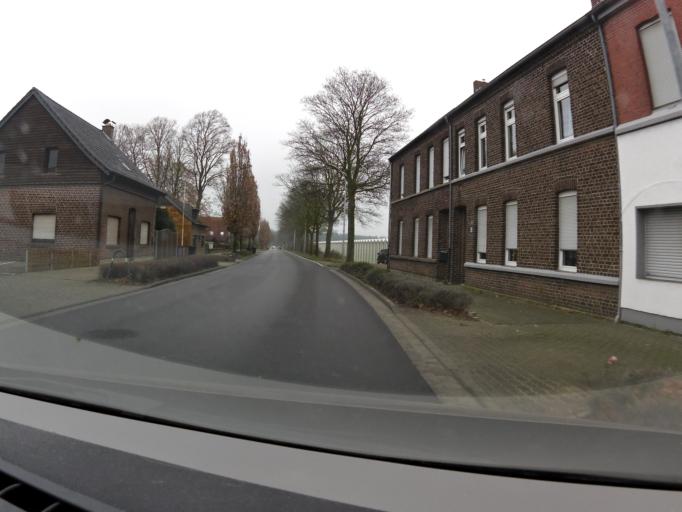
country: DE
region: North Rhine-Westphalia
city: Straelen
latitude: 51.4101
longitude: 6.2637
